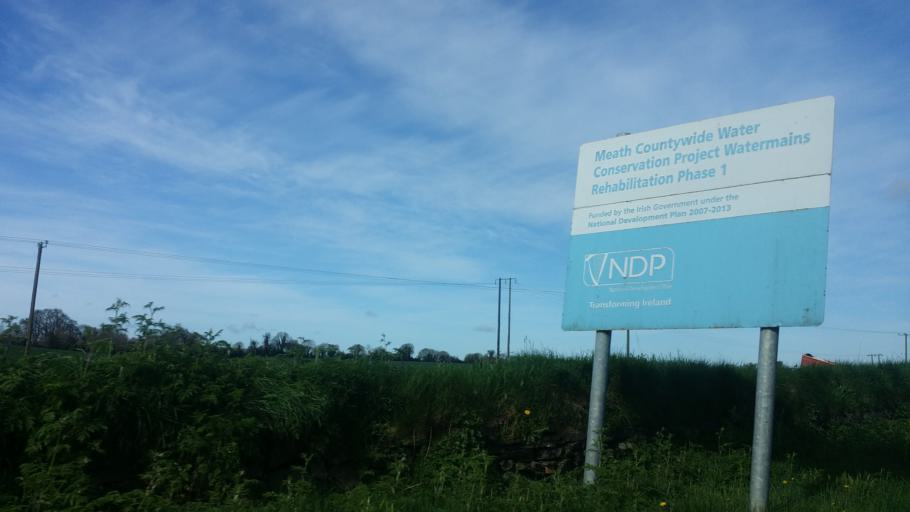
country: IE
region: Leinster
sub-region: An Mhi
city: Kells
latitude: 53.7216
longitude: -6.8518
